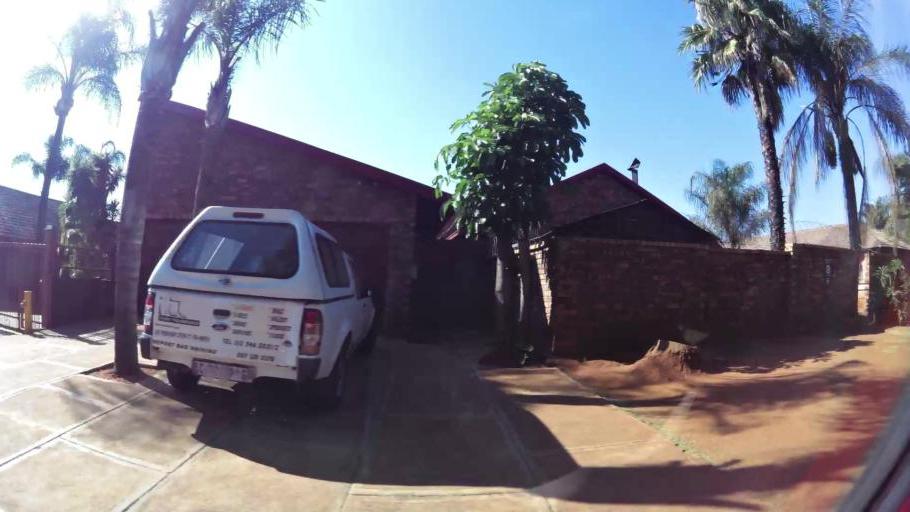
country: ZA
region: North-West
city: Ga-Rankuwa
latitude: -25.6485
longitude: 28.1117
